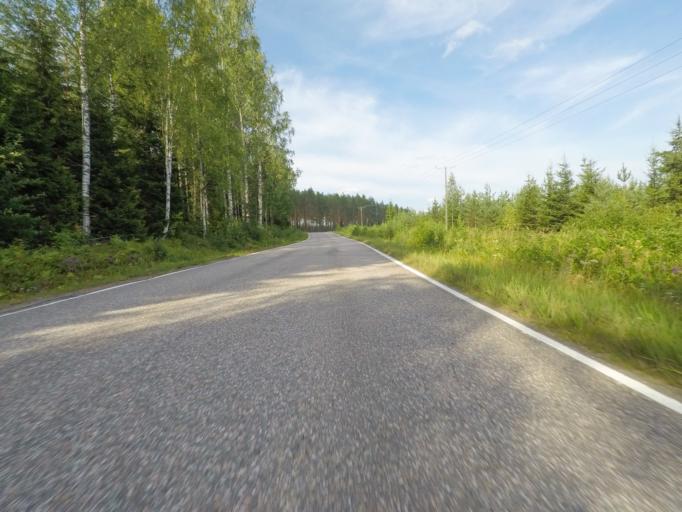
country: FI
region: Southern Savonia
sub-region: Savonlinna
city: Sulkava
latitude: 61.7284
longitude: 28.2058
